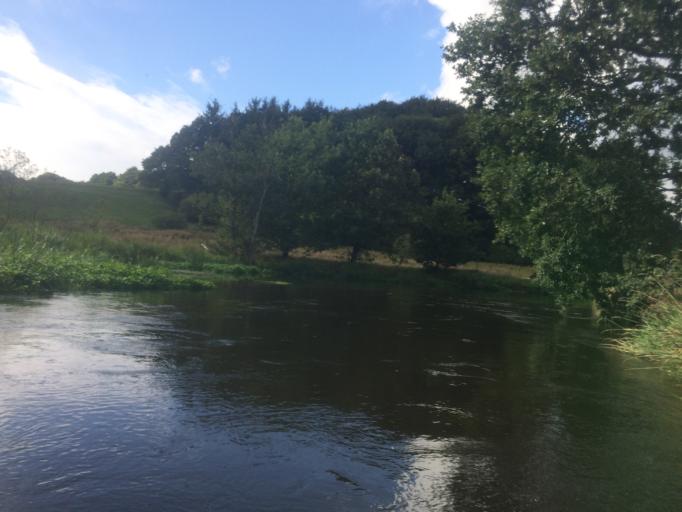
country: DK
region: South Denmark
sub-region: Vejle Kommune
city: Egtved
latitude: 55.6568
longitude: 9.3139
